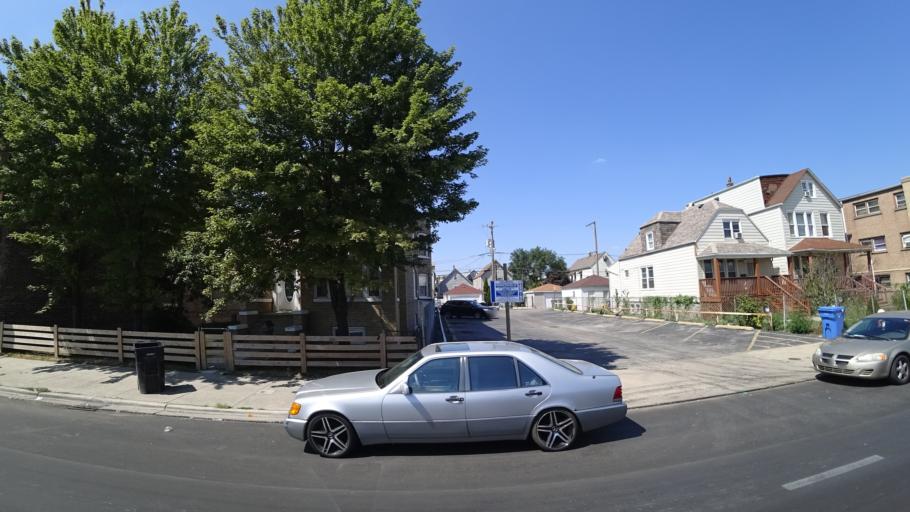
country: US
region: Illinois
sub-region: Cook County
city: Cicero
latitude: 41.8609
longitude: -87.7446
